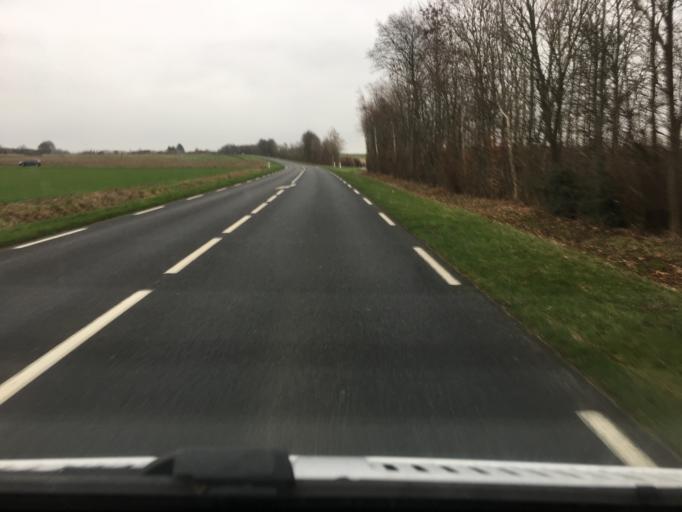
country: FR
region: Picardie
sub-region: Departement de la Somme
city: Saint-Valery-sur-Somme
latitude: 50.1750
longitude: 1.6177
